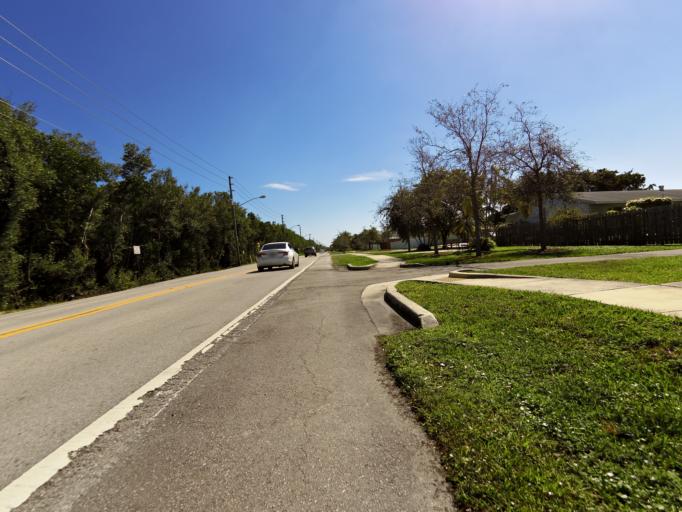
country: US
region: Florida
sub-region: Broward County
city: Dania Beach
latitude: 26.0444
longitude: -80.1353
